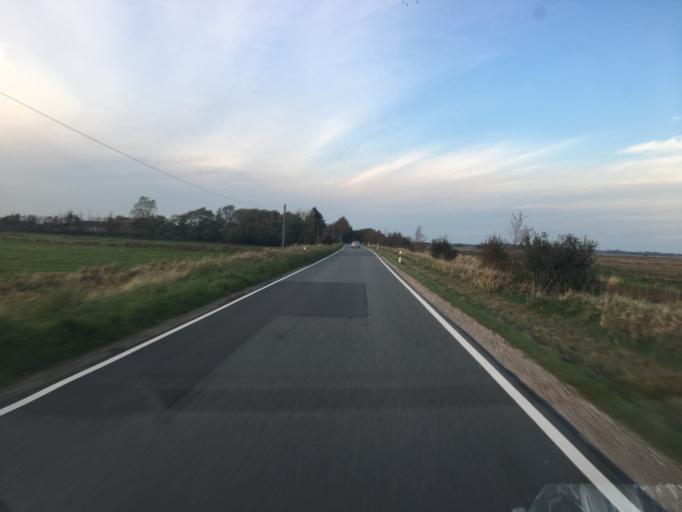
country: DE
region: Schleswig-Holstein
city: Humptrup
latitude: 54.8911
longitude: 8.8485
